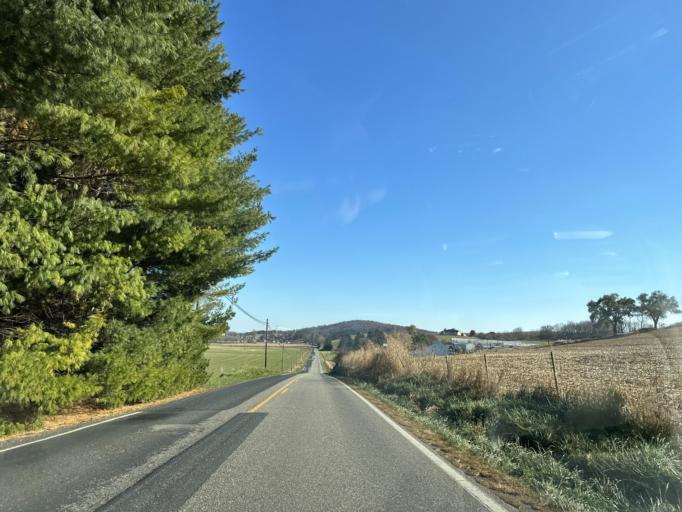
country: US
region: Virginia
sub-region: Rockingham County
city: Bridgewater
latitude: 38.3937
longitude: -79.0284
